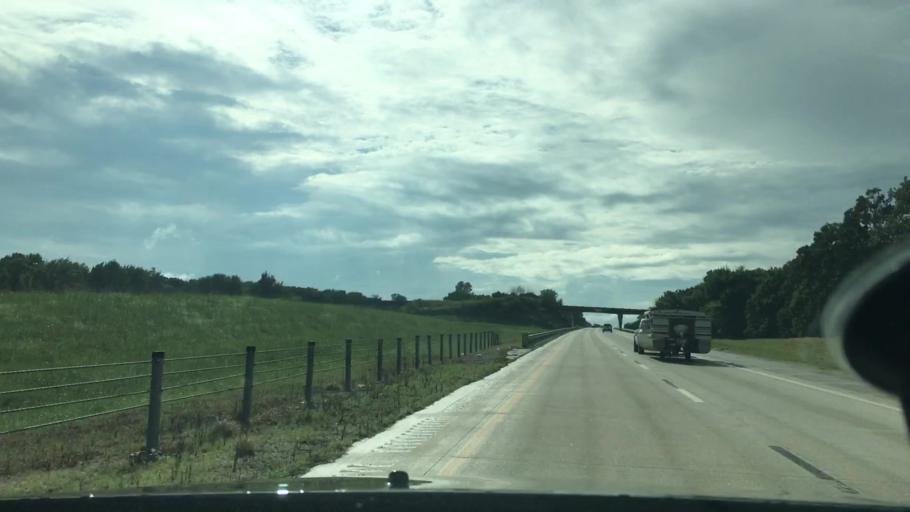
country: US
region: Oklahoma
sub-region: Lincoln County
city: Prague
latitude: 35.3853
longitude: -96.6150
